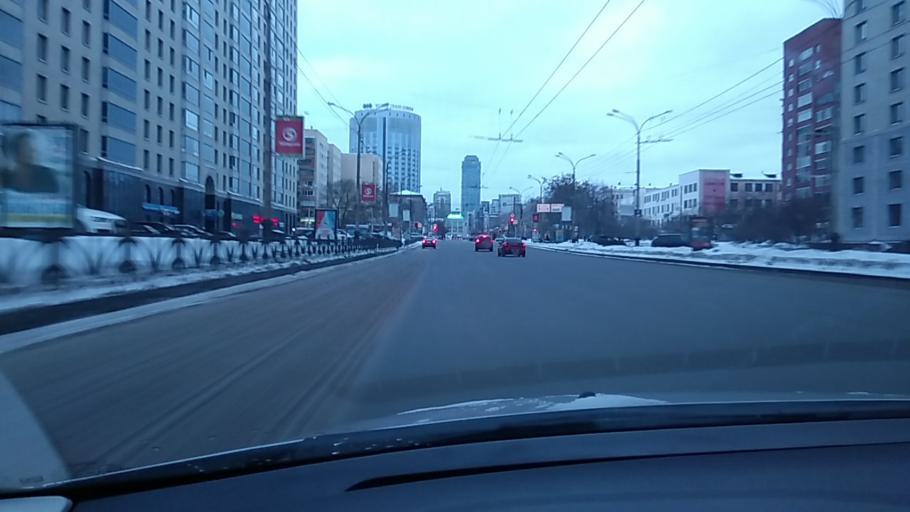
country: RU
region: Sverdlovsk
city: Yekaterinburg
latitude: 56.8225
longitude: 60.6185
